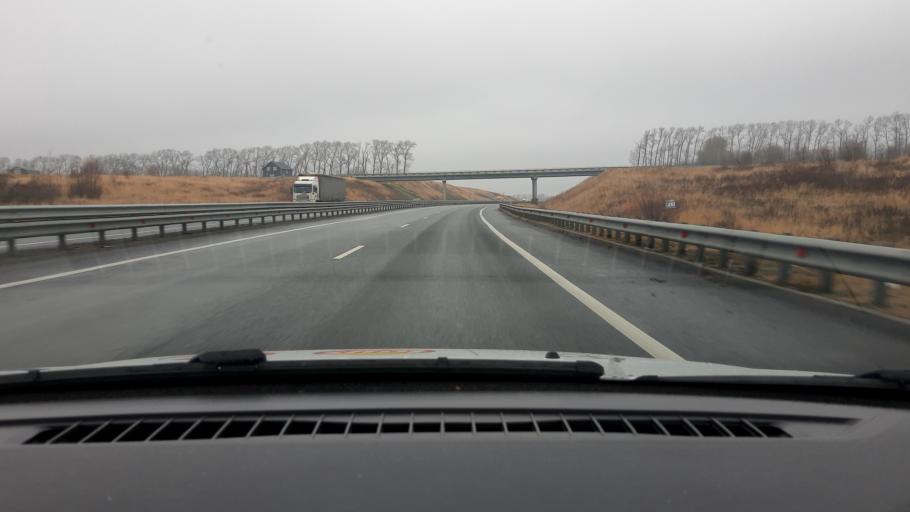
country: RU
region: Nizjnij Novgorod
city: Burevestnik
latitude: 56.1491
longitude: 43.7504
